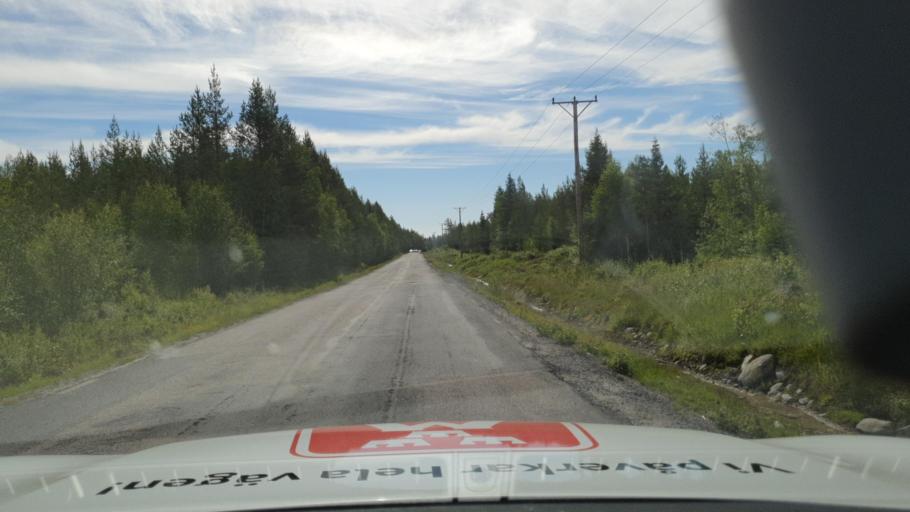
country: SE
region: Vaesterbotten
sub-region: Umea Kommun
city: Saevar
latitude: 63.8688
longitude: 20.7272
